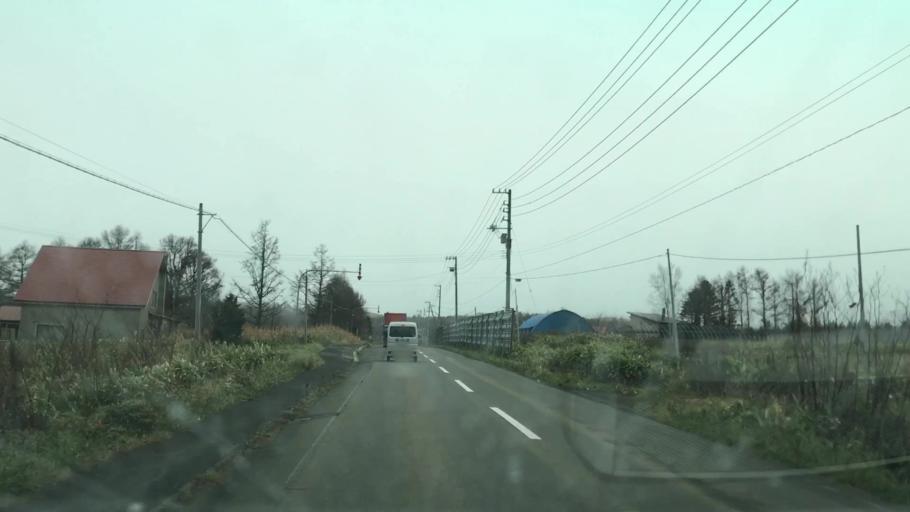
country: JP
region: Hokkaido
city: Yoichi
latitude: 43.3090
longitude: 140.5515
